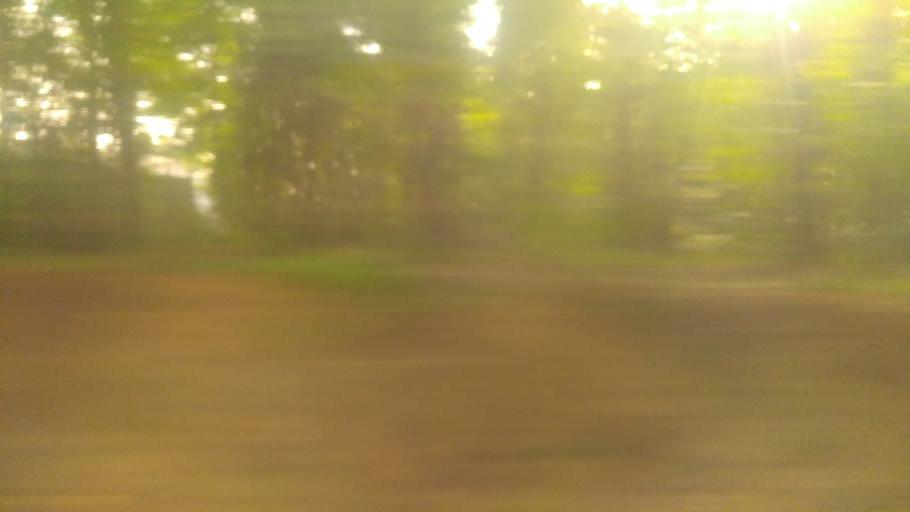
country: US
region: North Carolina
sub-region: Wake County
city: Raleigh
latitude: 35.7382
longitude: -78.6367
